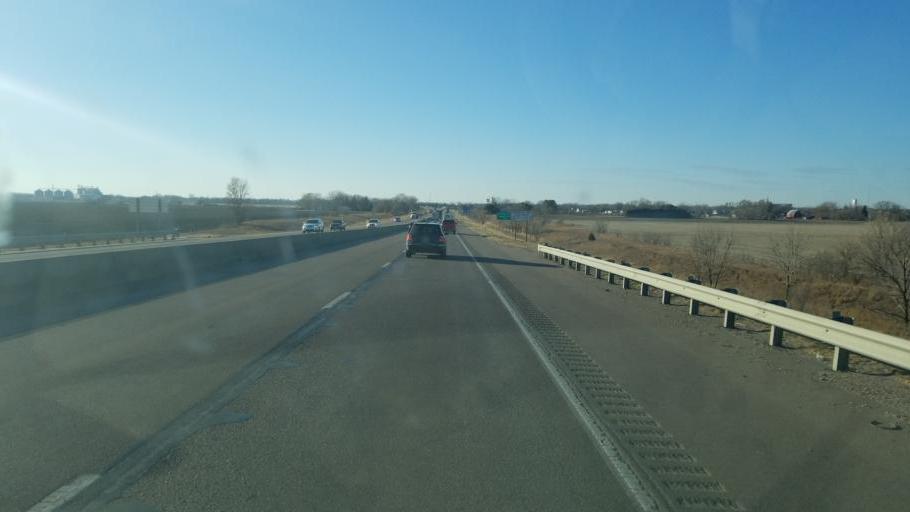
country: US
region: Nebraska
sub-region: Dakota County
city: South Sioux City
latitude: 42.4477
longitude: -96.3861
